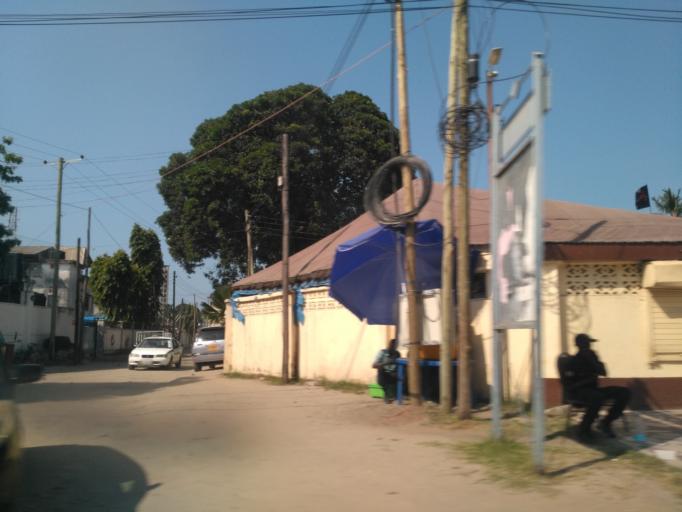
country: TZ
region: Dar es Salaam
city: Dar es Salaam
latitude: -6.8088
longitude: 39.2835
